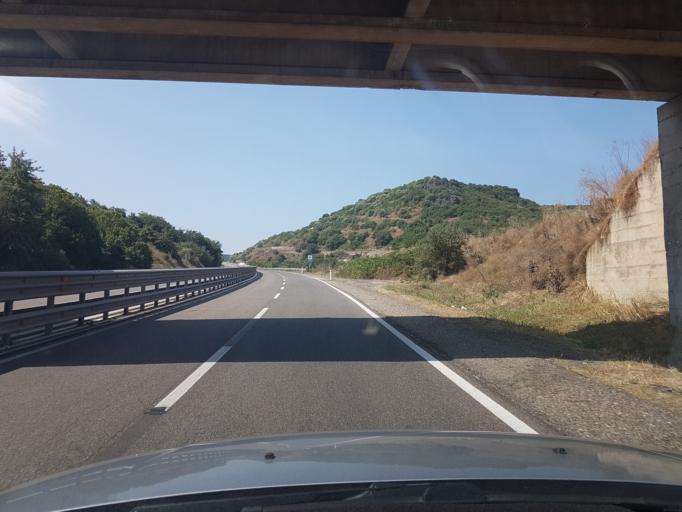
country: IT
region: Sardinia
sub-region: Provincia di Oristano
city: Soddi
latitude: 40.1431
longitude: 8.8737
